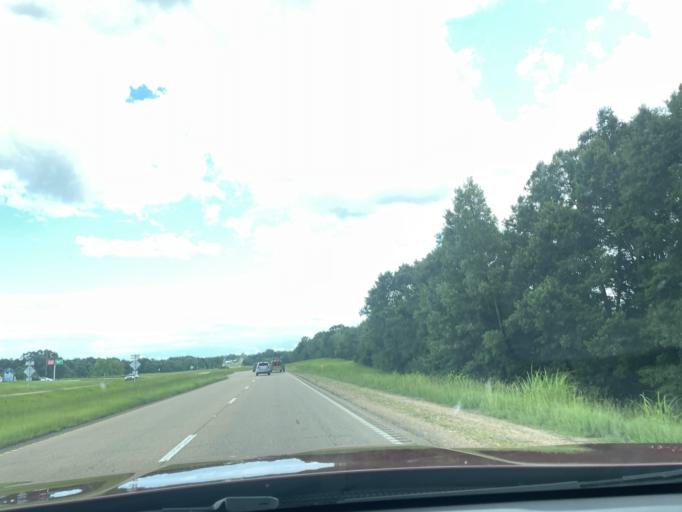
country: US
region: Mississippi
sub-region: Madison County
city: Flora
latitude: 32.5503
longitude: -90.3215
